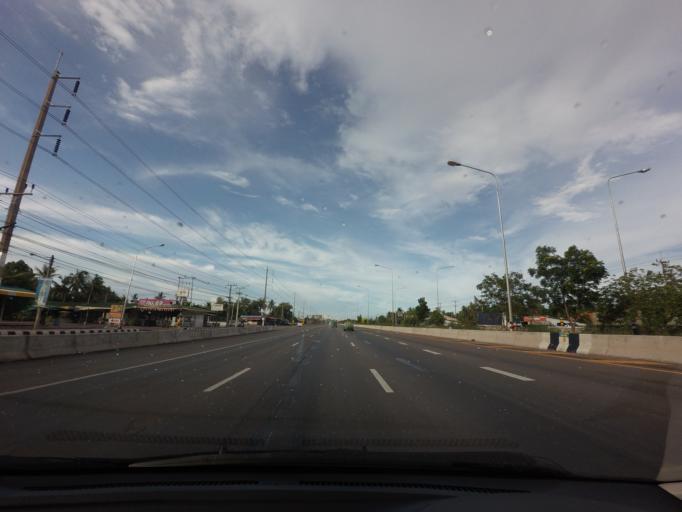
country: TH
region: Samut Songkhram
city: Amphawa
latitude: 13.3758
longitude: 99.9641
